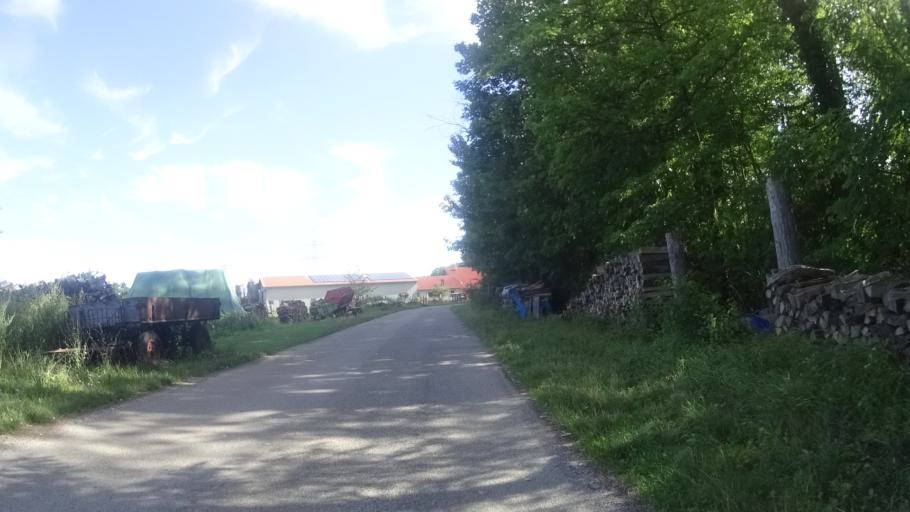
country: DE
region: Rheinland-Pfalz
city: Worth am Rhein
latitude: 49.0592
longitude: 8.2726
